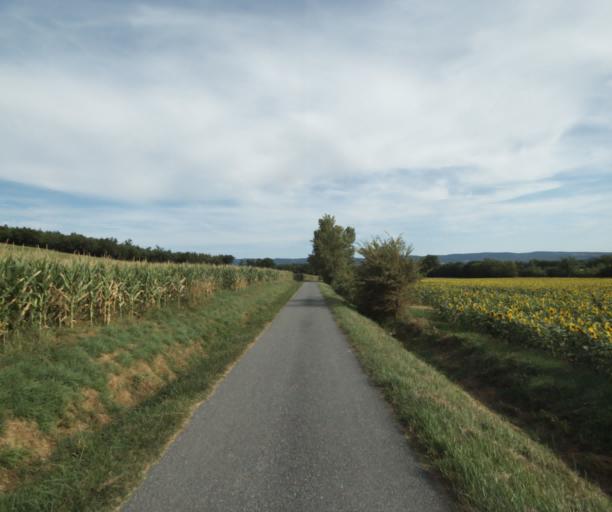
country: FR
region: Midi-Pyrenees
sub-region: Departement du Tarn
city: Puylaurens
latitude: 43.5316
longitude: 2.0451
